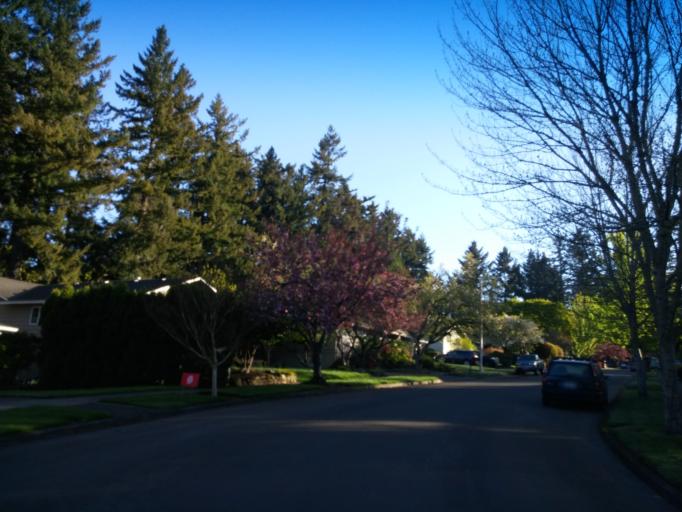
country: US
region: Oregon
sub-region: Washington County
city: Cedar Hills
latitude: 45.5062
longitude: -122.7885
